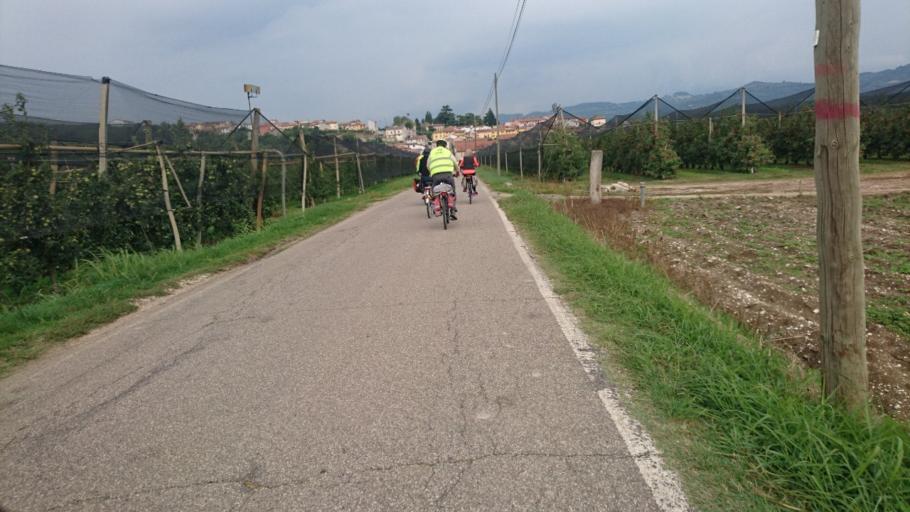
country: IT
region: Veneto
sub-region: Provincia di Verona
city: Soave
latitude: 45.4249
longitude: 11.2215
